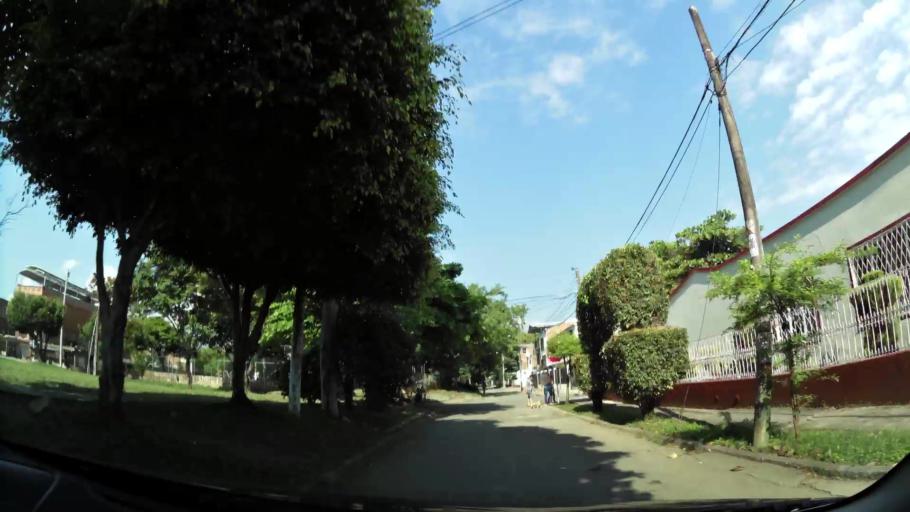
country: CO
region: Valle del Cauca
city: Cali
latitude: 3.4206
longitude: -76.5139
